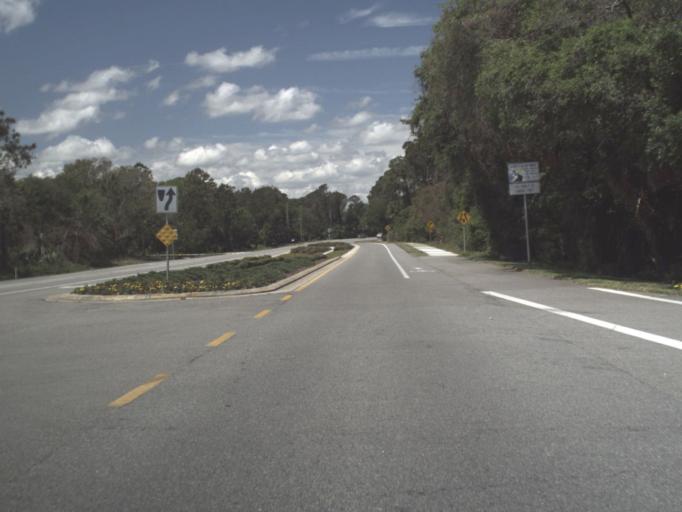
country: US
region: Florida
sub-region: Flagler County
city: Palm Coast
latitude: 29.5633
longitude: -81.1737
